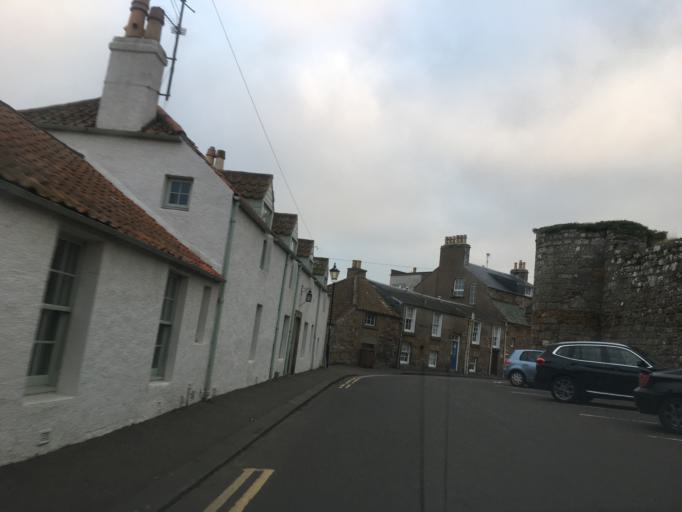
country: GB
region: Scotland
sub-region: Fife
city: Saint Andrews
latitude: 56.3371
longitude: -2.7841
